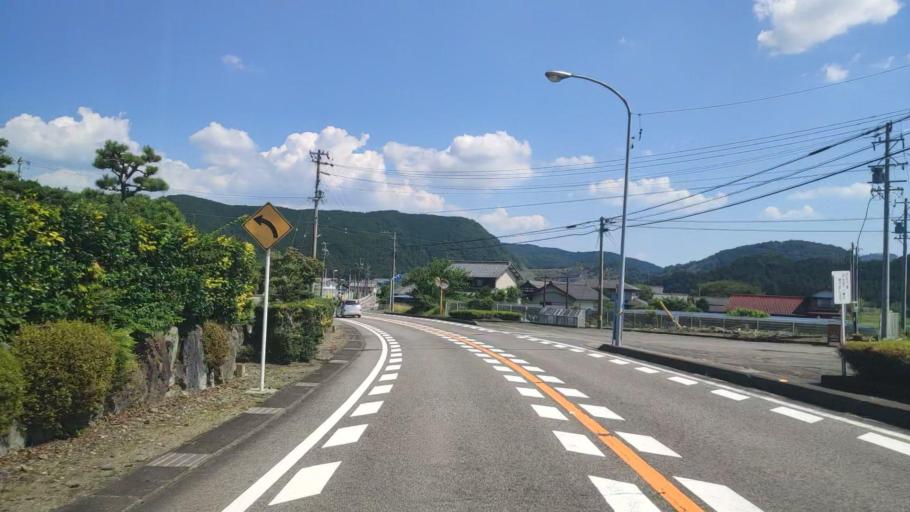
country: JP
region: Gifu
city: Godo
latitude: 35.5404
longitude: 136.6444
